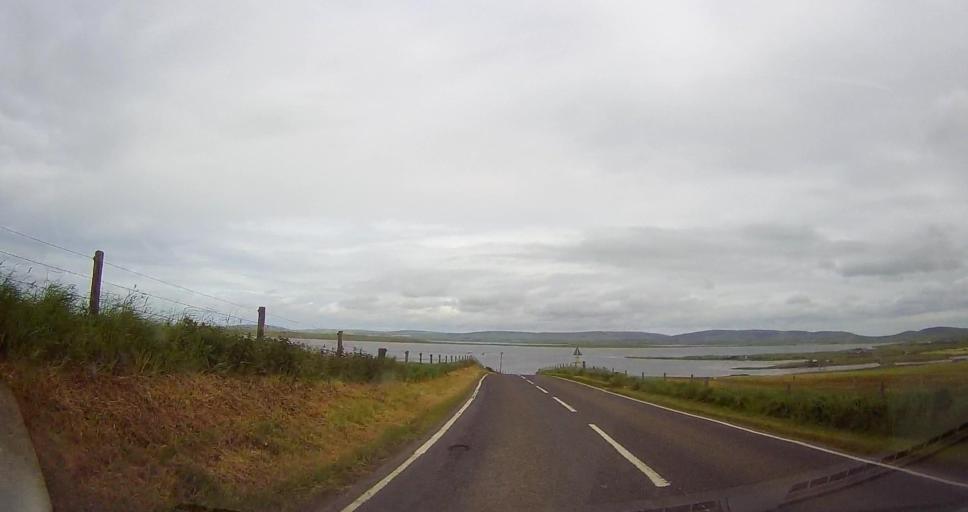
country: GB
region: Scotland
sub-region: Orkney Islands
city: Stromness
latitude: 58.9797
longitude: -3.2644
